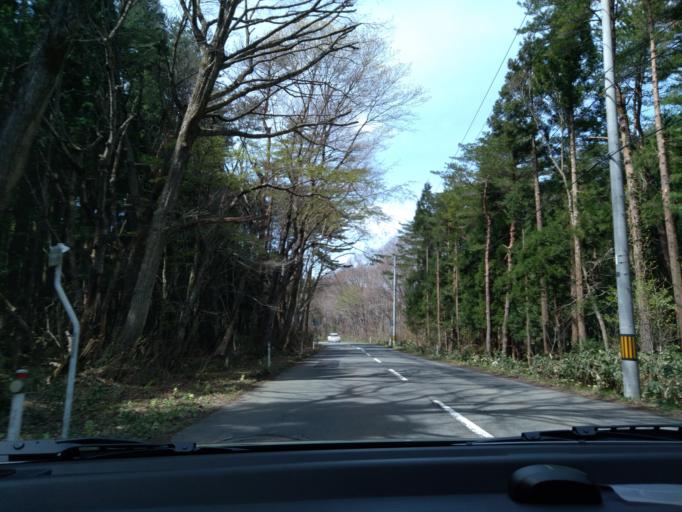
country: JP
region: Iwate
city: Kitakami
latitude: 39.2525
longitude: 140.9824
